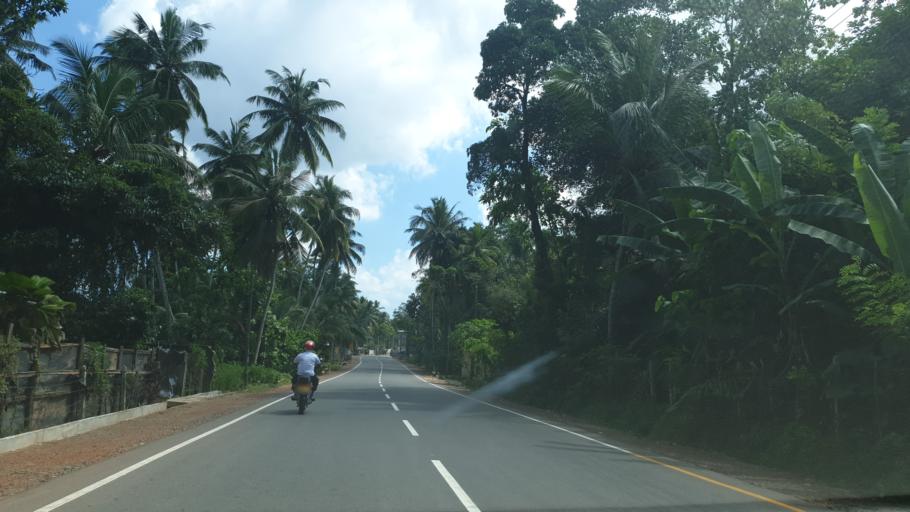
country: LK
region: Western
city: Panadura
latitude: 6.6700
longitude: 79.9423
